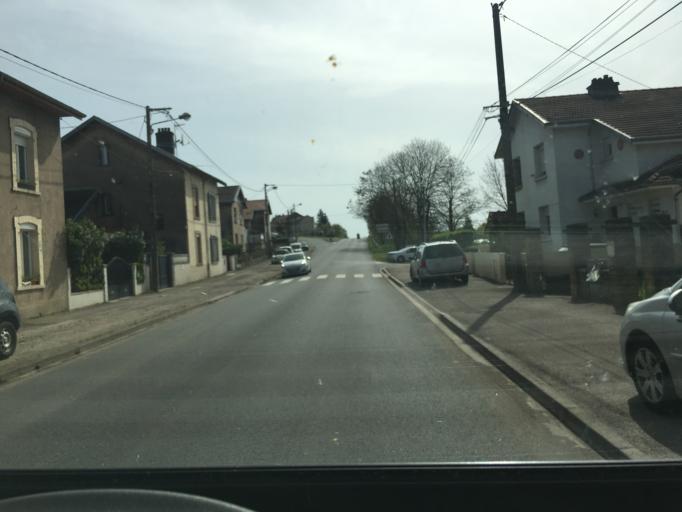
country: FR
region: Lorraine
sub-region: Departement de Meurthe-et-Moselle
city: Chavigny
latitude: 48.6131
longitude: 6.1220
